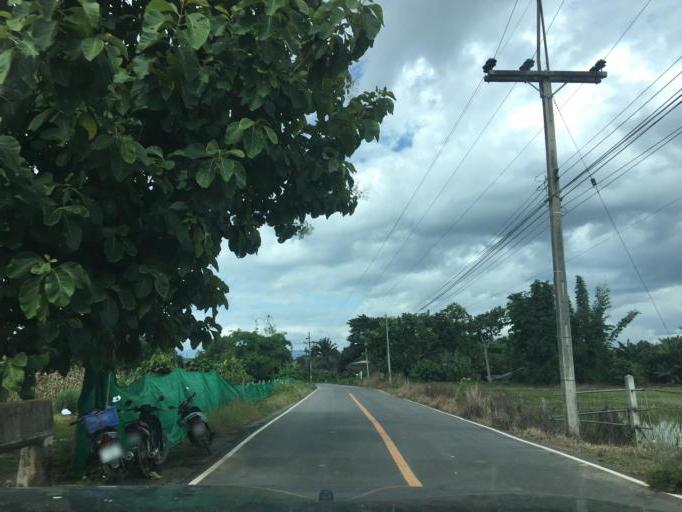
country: TH
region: Chiang Rai
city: Wiang Pa Pao
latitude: 19.2321
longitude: 99.5107
